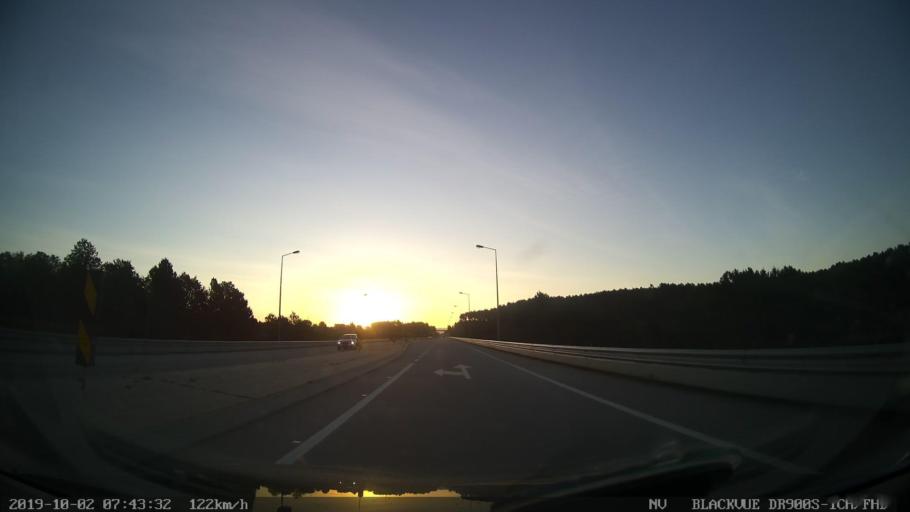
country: PT
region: Vila Real
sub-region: Sabrosa
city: Vilela
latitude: 41.2659
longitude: -7.6372
